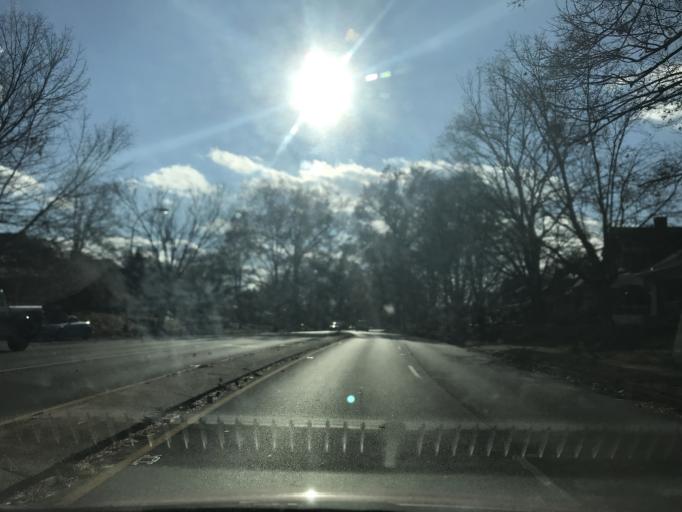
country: US
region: Kentucky
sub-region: Jefferson County
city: Audubon Park
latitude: 38.2234
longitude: -85.7306
